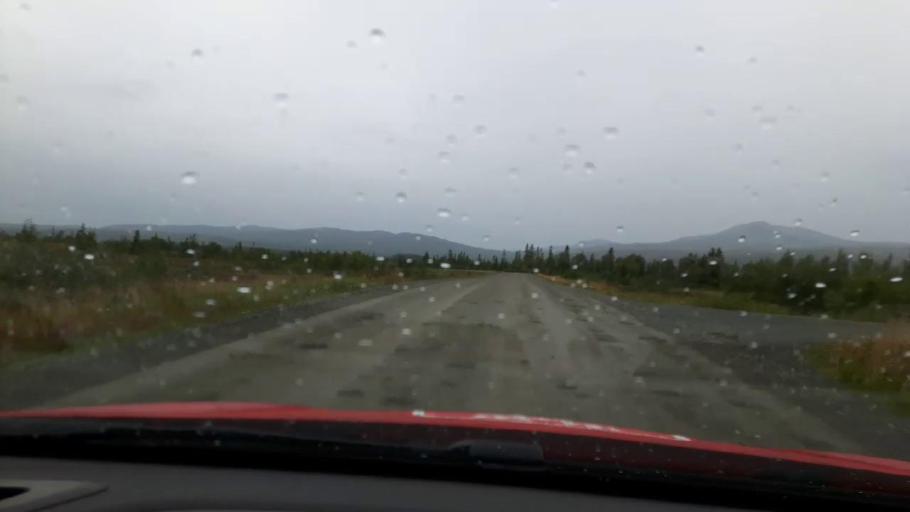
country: NO
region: Nord-Trondelag
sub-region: Meraker
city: Meraker
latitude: 63.5957
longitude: 12.2756
